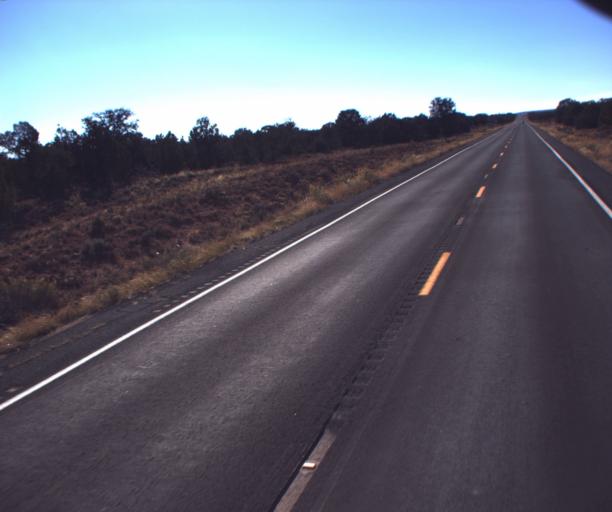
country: US
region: Arizona
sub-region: Coconino County
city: Kaibito
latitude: 36.5828
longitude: -110.8376
